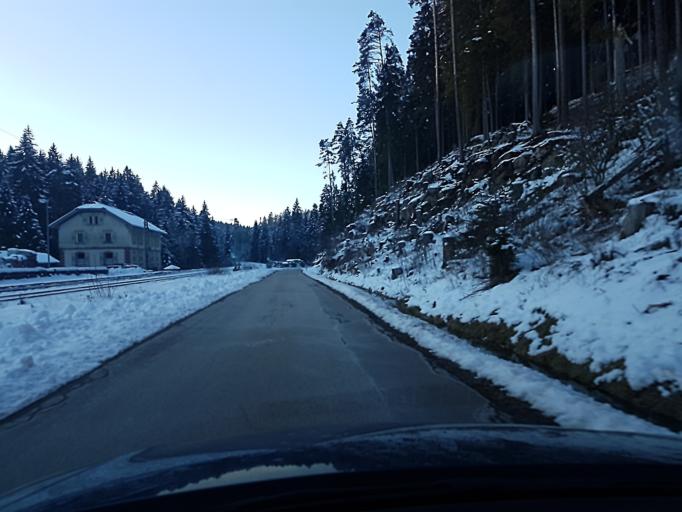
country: DE
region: Baden-Wuerttemberg
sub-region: Freiburg Region
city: Monchweiler
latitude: 48.0732
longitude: 8.4176
